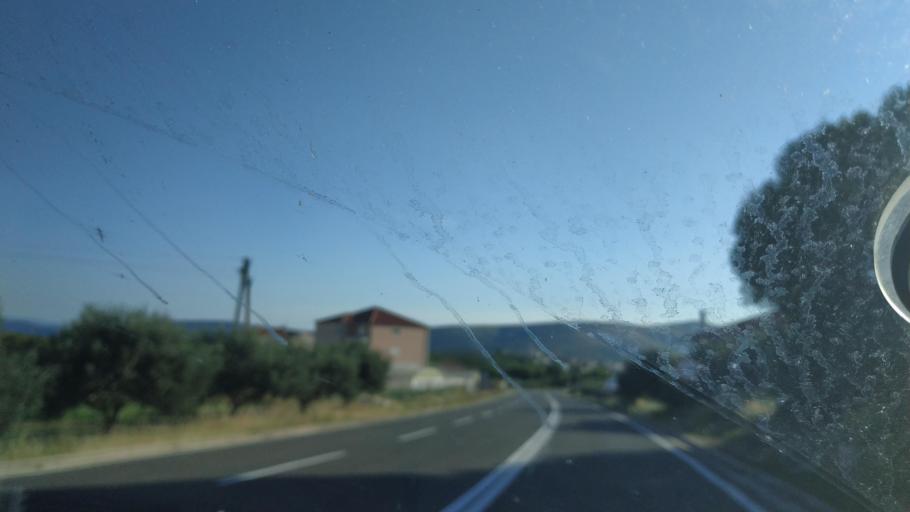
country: HR
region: Splitsko-Dalmatinska
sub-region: Grad Trogir
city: Trogir
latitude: 43.5157
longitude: 16.1976
